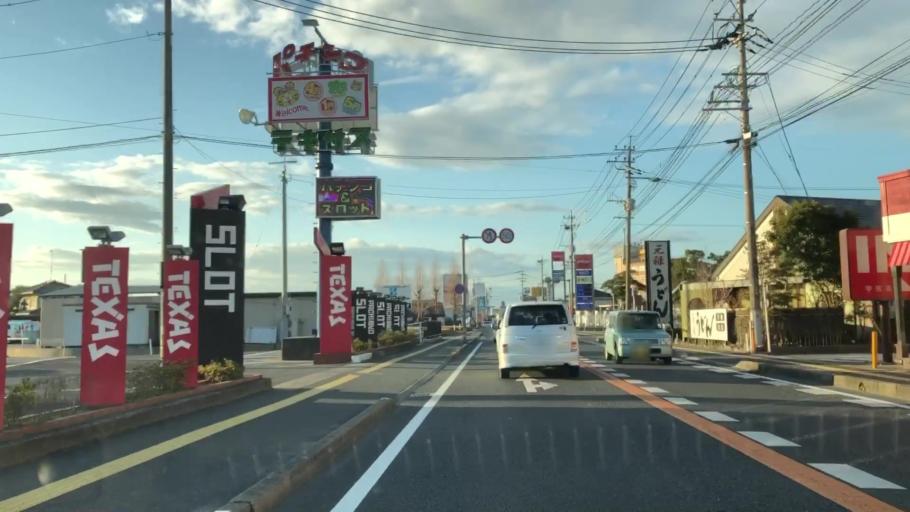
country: JP
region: Oita
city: Bungo-Takada-shi
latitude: 33.5276
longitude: 131.3403
